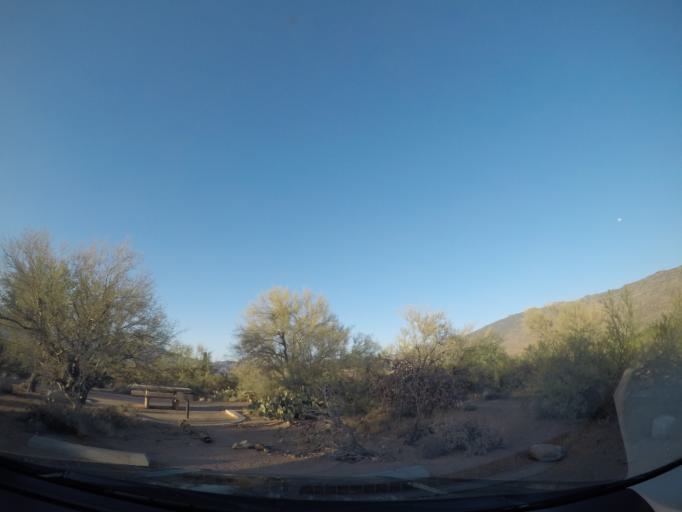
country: US
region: Arizona
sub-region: Pima County
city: Tanque Verde
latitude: 32.2114
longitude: -110.7245
